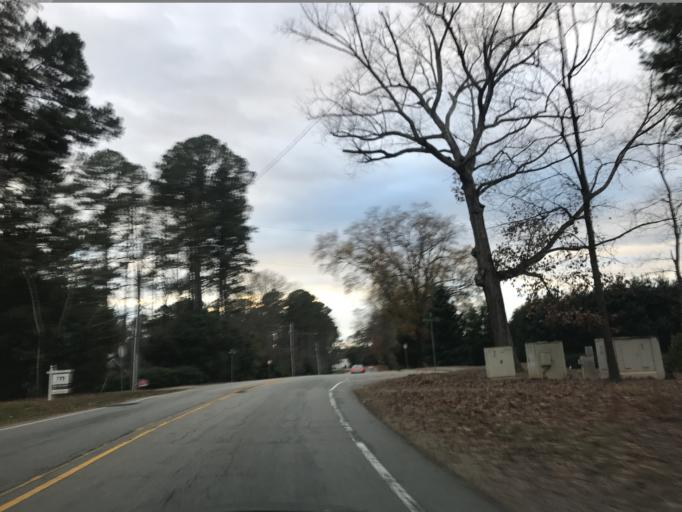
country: US
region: North Carolina
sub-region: Wake County
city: West Raleigh
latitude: 35.8303
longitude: -78.6864
